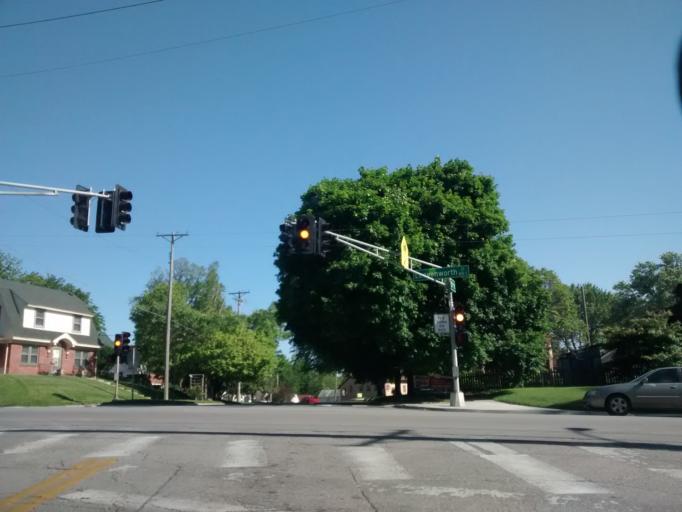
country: US
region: Nebraska
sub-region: Douglas County
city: Ralston
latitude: 41.2526
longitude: -96.0019
